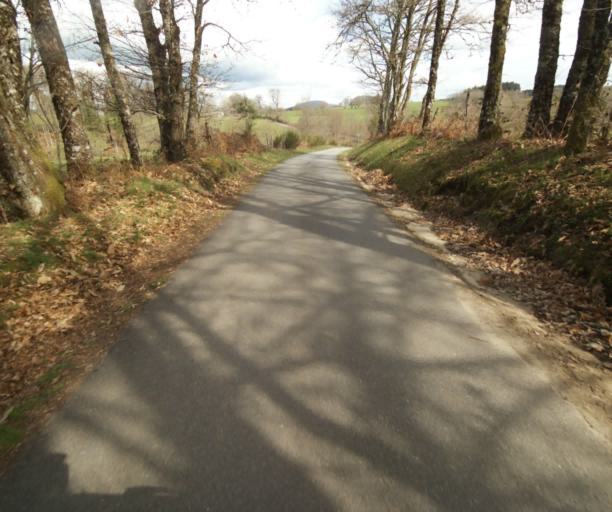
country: FR
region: Limousin
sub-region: Departement de la Correze
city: Correze
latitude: 45.3621
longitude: 1.8985
